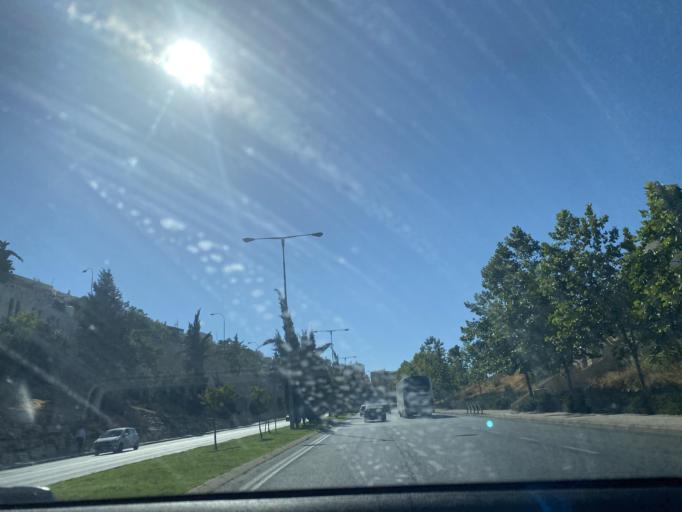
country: PS
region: West Bank
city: Bayt Iksa
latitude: 31.8195
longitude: 35.1924
